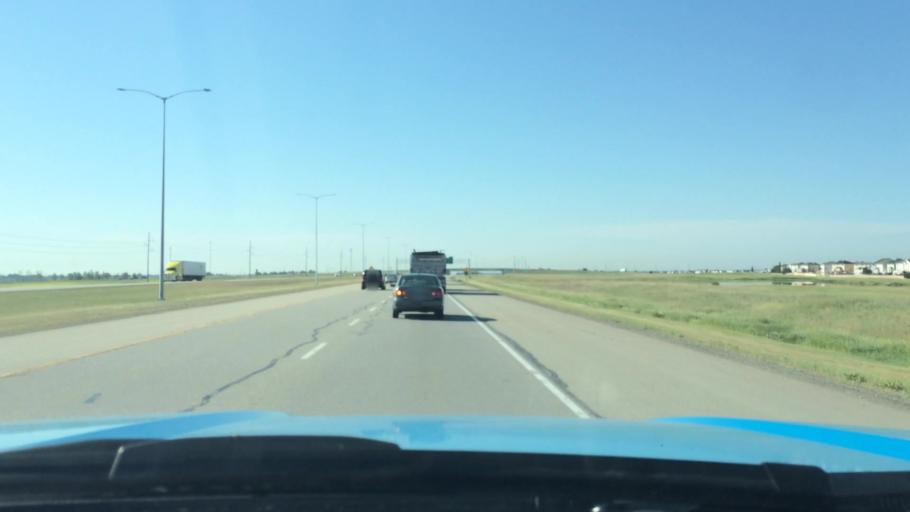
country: CA
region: Alberta
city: Chestermere
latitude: 51.1082
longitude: -113.9201
